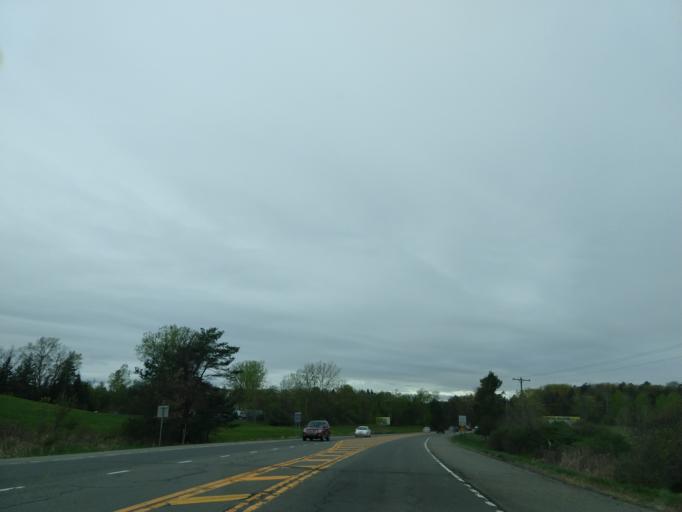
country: US
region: New York
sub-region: Tompkins County
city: Northeast Ithaca
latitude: 42.4687
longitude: -76.4106
